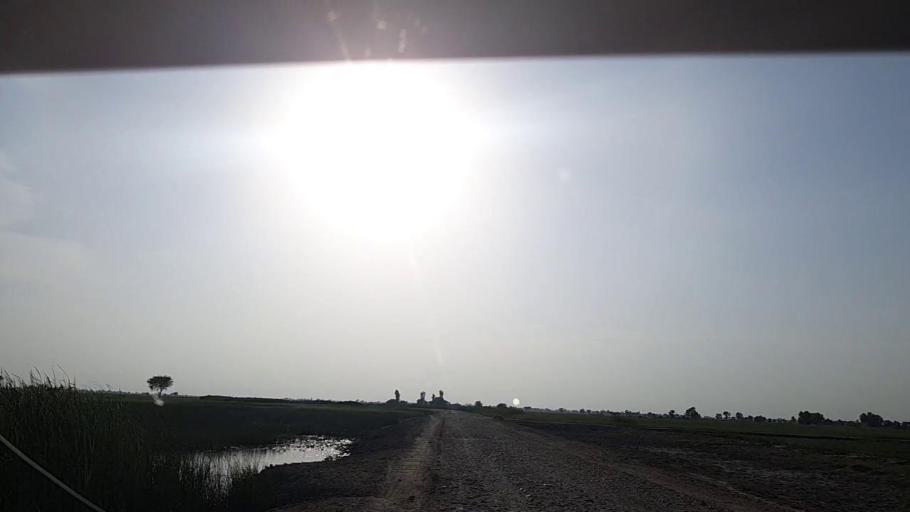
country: PK
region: Sindh
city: Khanpur
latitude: 27.8355
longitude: 69.3723
